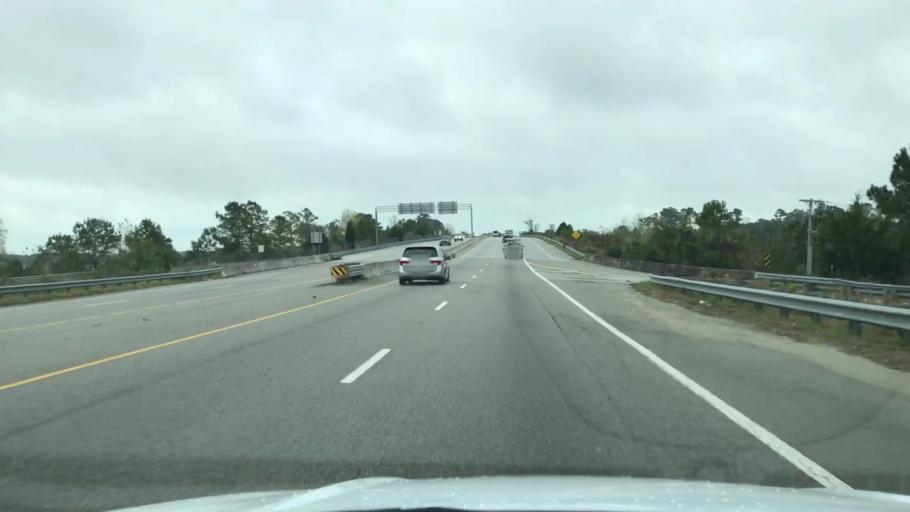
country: US
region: South Carolina
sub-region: Horry County
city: Myrtle Beach
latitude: 33.7528
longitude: -78.8517
